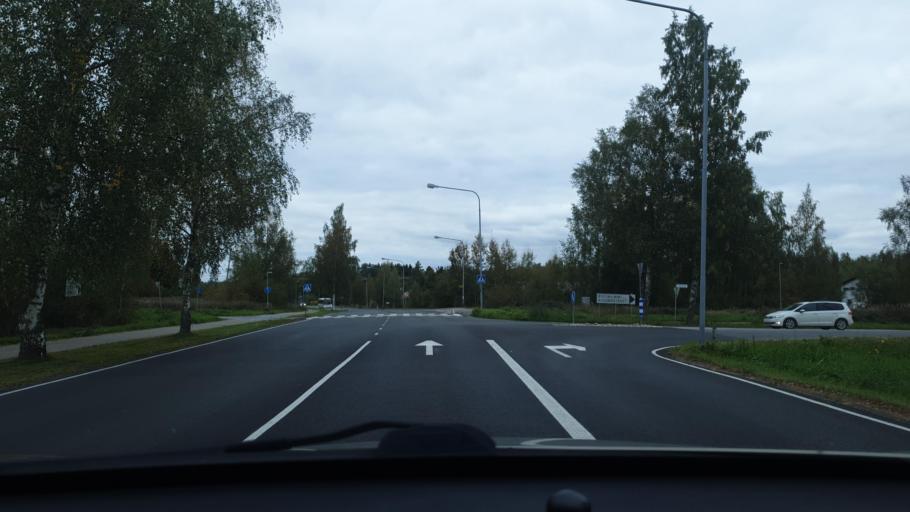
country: FI
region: Ostrobothnia
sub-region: Vaasa
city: Teeriniemi
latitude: 63.0890
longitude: 21.6998
